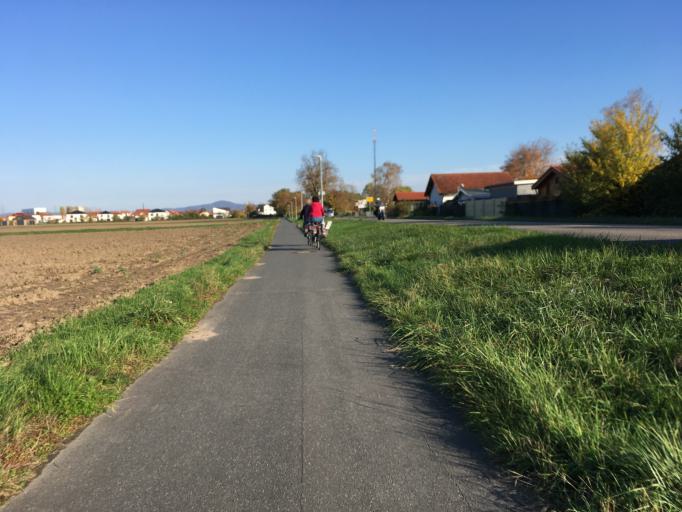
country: DE
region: Hesse
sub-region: Regierungsbezirk Darmstadt
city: Biblis
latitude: 49.6863
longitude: 8.4322
